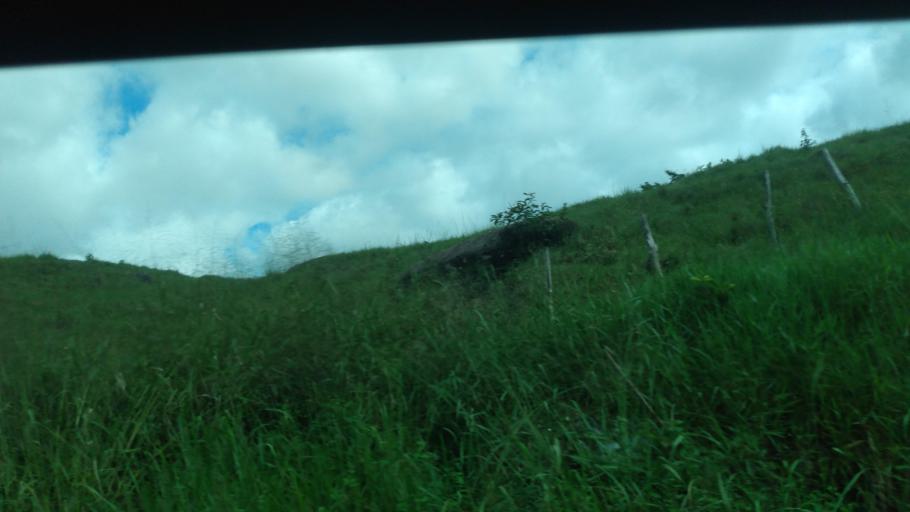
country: BR
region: Pernambuco
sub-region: Quipapa
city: Quipapa
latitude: -8.8048
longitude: -36.0075
